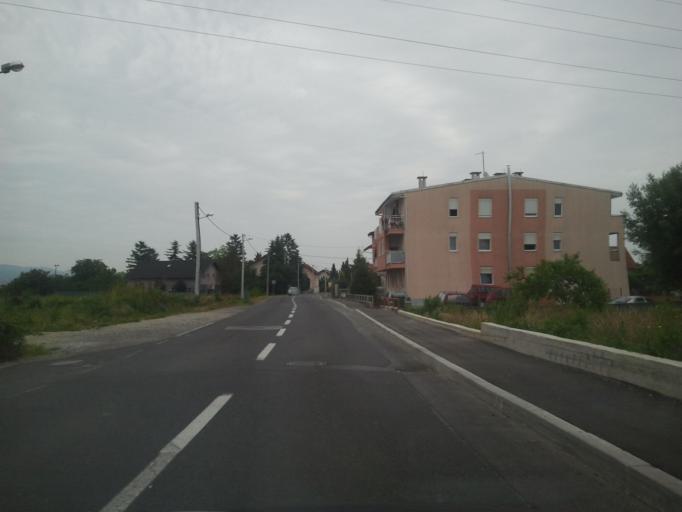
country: HR
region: Grad Zagreb
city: Zadvorsko
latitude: 45.7533
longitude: 15.9273
